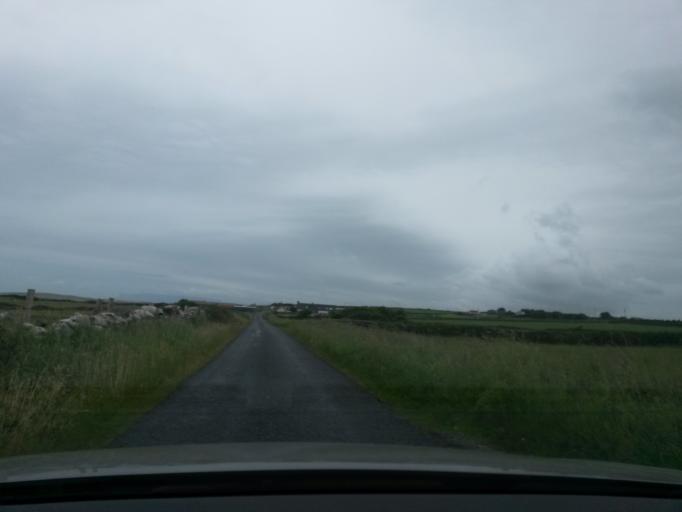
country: IE
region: Connaught
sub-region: Sligo
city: Tobercurry
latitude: 54.2523
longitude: -8.8217
